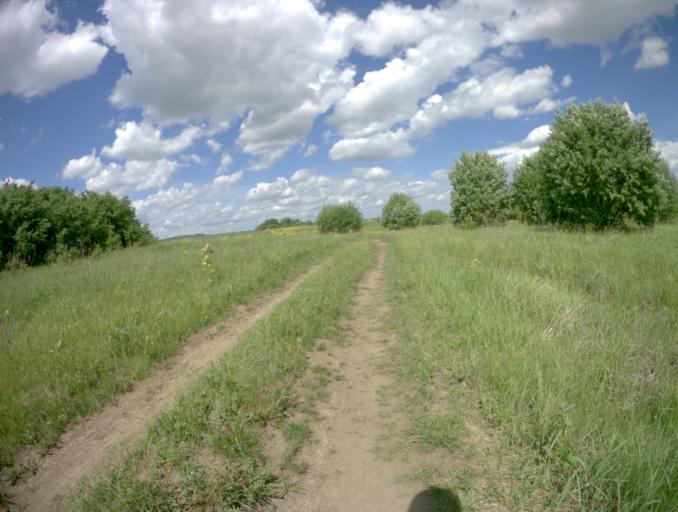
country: RU
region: Ivanovo
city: Gavrilov Posad
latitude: 56.4391
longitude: 40.2482
